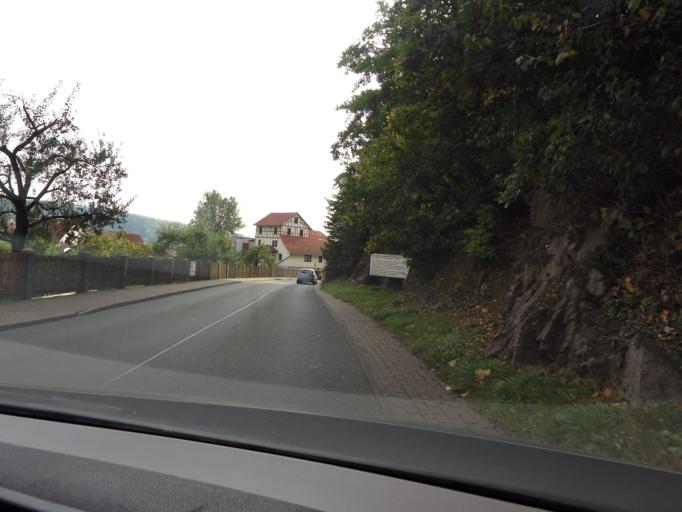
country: DE
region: Thuringia
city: Trusetal
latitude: 50.7889
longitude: 10.4088
